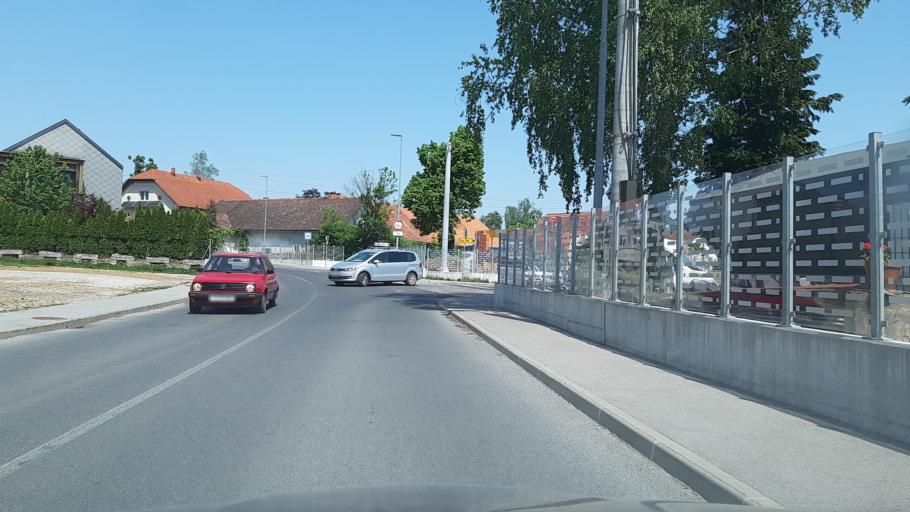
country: SI
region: Brezovica
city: Notranje Gorice
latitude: 45.9740
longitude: 14.4205
